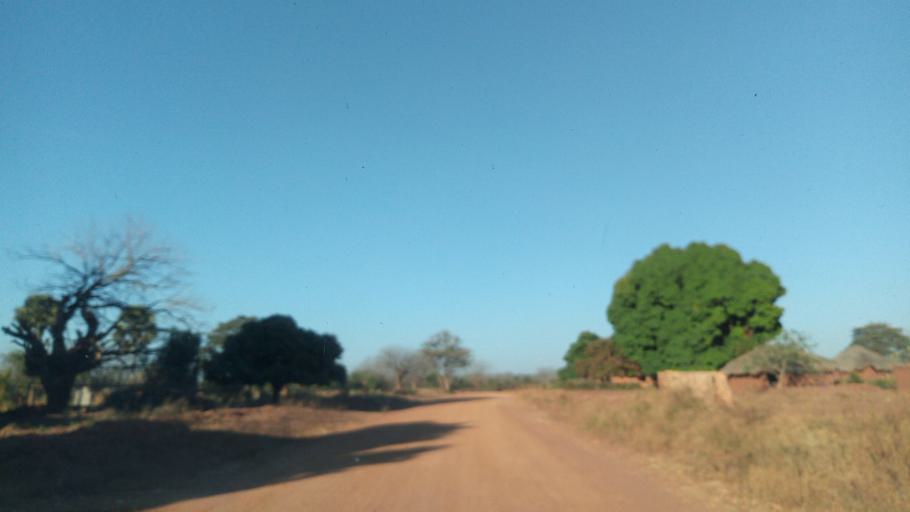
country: ZM
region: Luapula
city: Mwense
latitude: -10.4055
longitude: 28.6165
